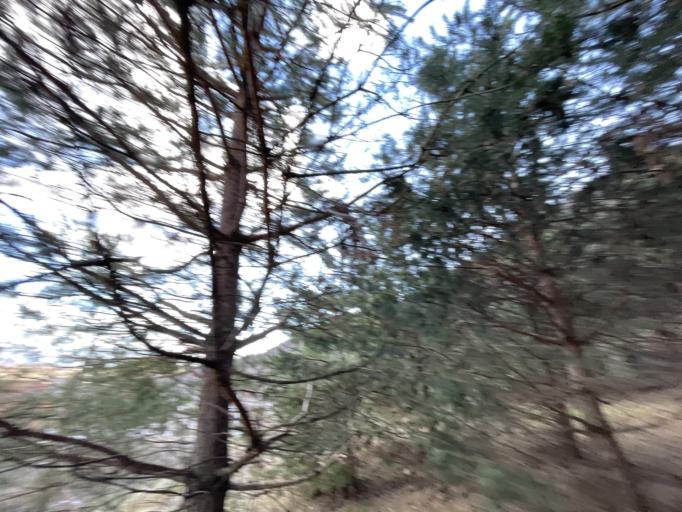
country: XK
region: Gjakova
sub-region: Komuna e Decanit
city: Strellc i Eperm
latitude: 42.5944
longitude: 20.2884
